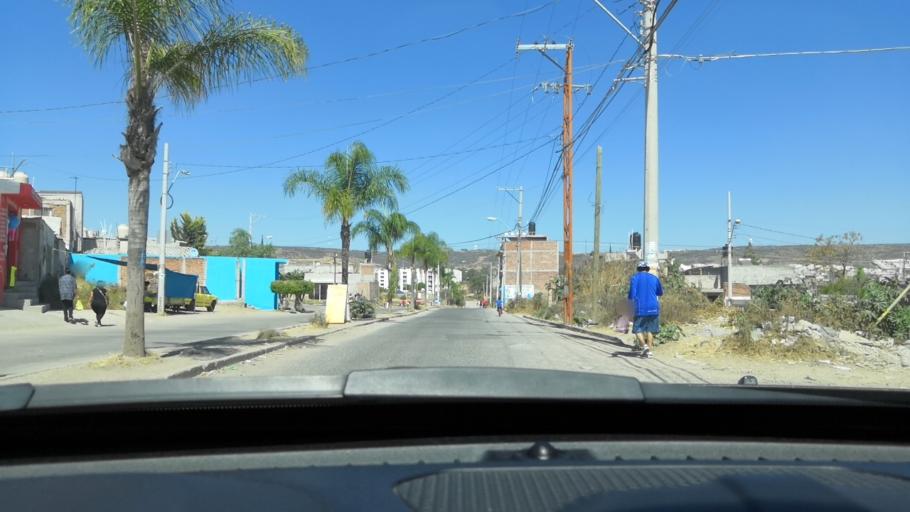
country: MX
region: Guanajuato
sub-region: Leon
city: Centro Familiar la Soledad
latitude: 21.1411
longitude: -101.7484
